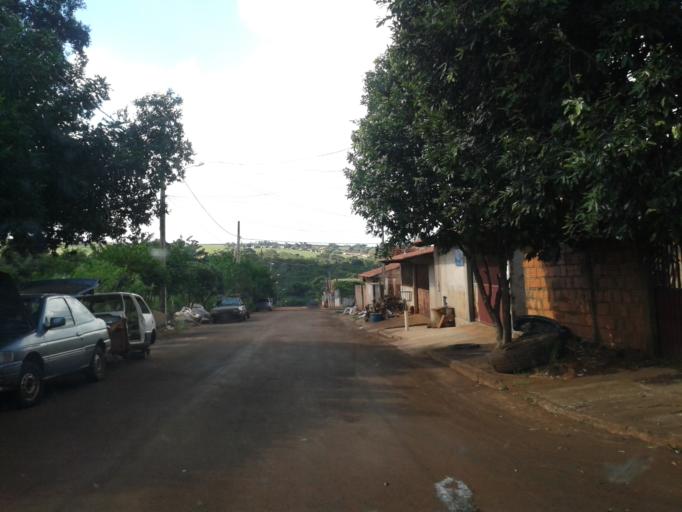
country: BR
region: Minas Gerais
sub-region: Capinopolis
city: Capinopolis
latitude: -18.6838
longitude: -49.5833
